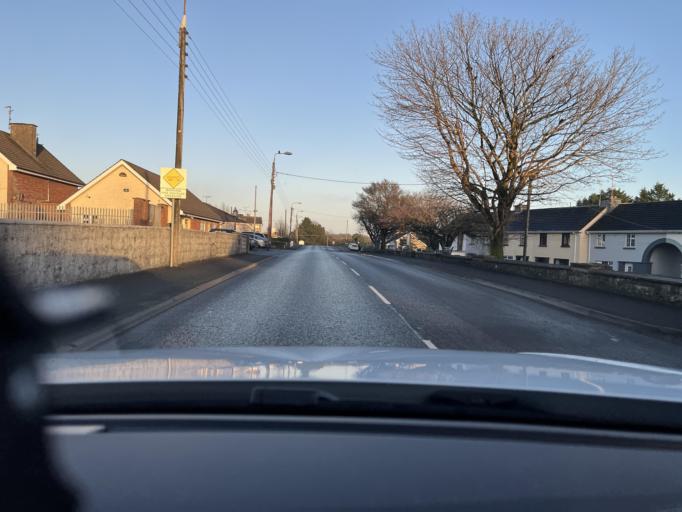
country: IE
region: Ulster
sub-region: An Cabhan
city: Ballyconnell
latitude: 54.1187
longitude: -7.5808
